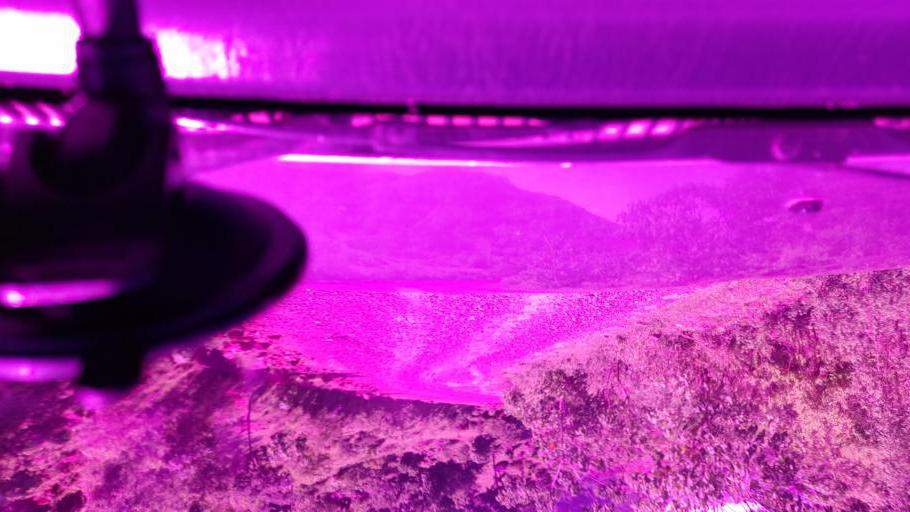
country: ET
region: Oromiya
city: Jima
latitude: 7.8304
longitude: 37.5463
